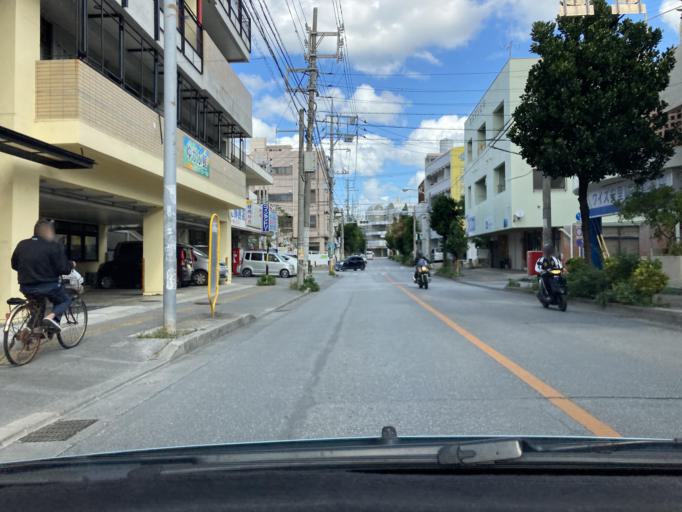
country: JP
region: Okinawa
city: Naha-shi
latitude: 26.2143
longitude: 127.6997
